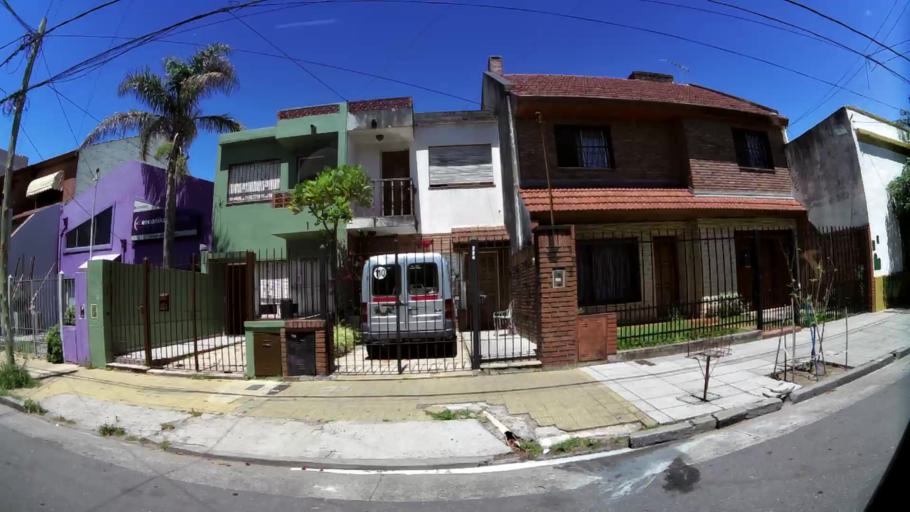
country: AR
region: Buenos Aires
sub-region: Partido de San Isidro
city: San Isidro
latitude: -34.4944
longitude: -58.5108
